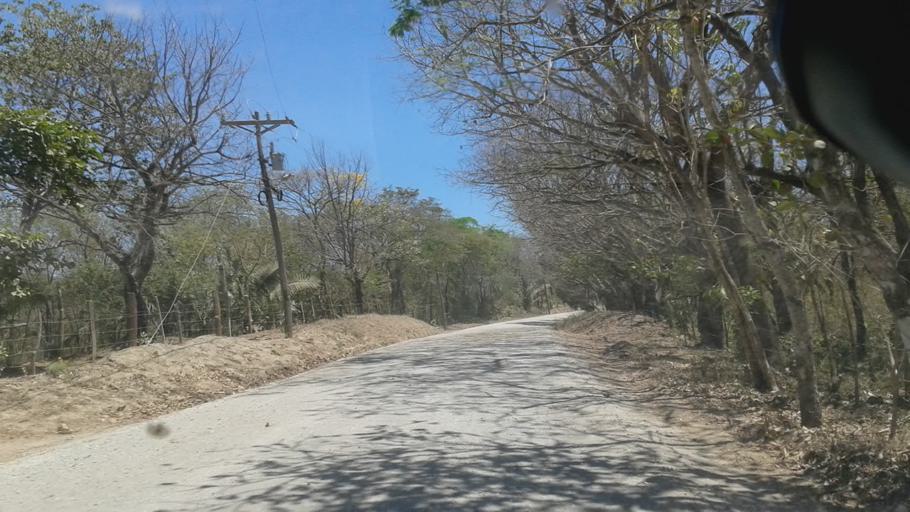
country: CR
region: Guanacaste
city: Samara
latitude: 10.0157
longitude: -85.7195
